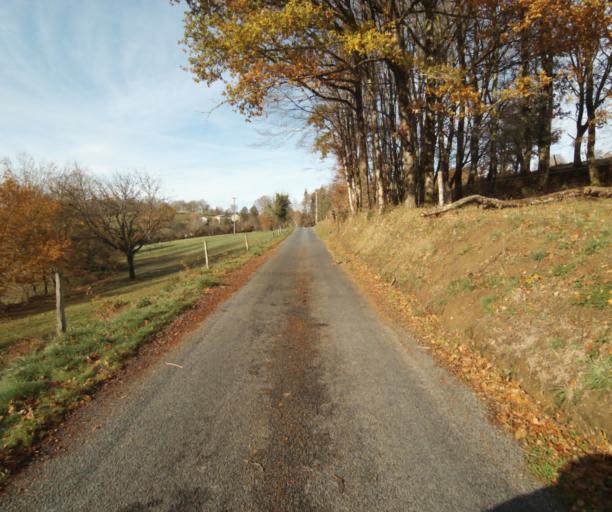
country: FR
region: Limousin
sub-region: Departement de la Correze
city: Chameyrat
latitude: 45.2286
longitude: 1.7315
